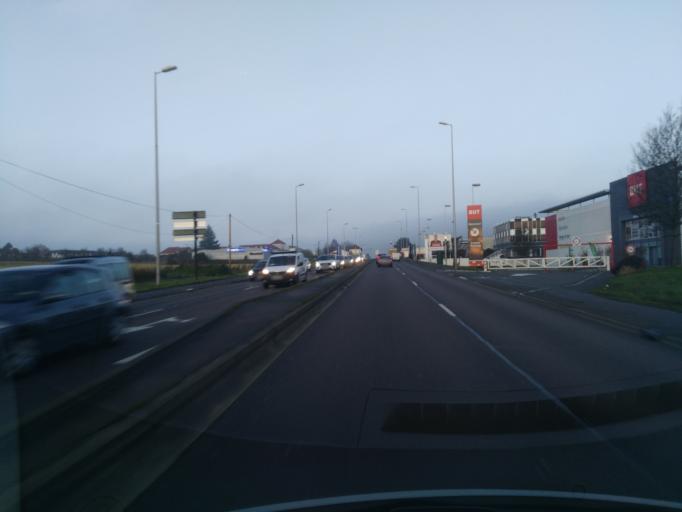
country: FR
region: Ile-de-France
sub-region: Departement des Yvelines
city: Orgeval
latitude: 48.9273
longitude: 1.9852
